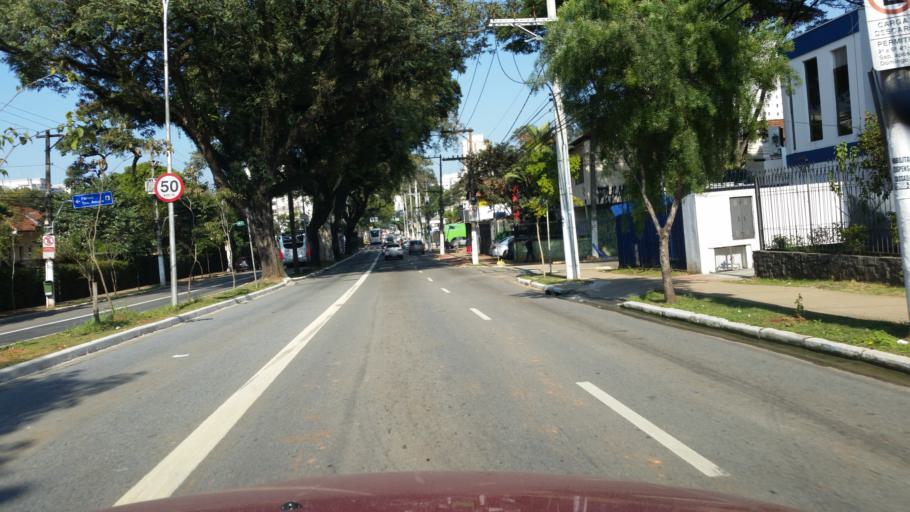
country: BR
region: Sao Paulo
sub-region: Diadema
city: Diadema
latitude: -23.6373
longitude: -46.6965
